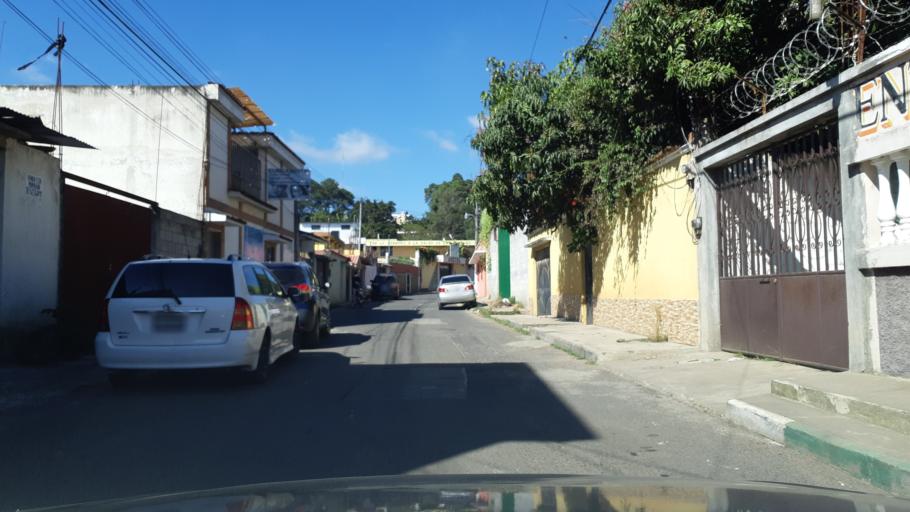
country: GT
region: Chimaltenango
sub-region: Municipio de Chimaltenango
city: Chimaltenango
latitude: 14.6544
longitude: -90.8156
